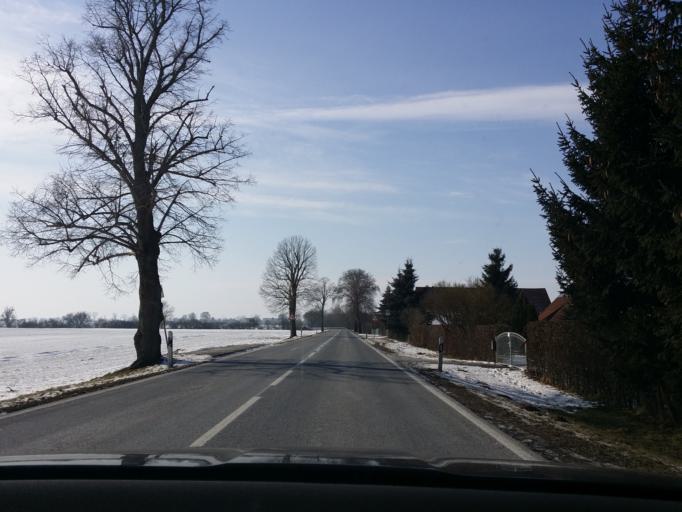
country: DE
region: Mecklenburg-Vorpommern
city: Wulkenzin
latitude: 53.5415
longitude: 13.1567
